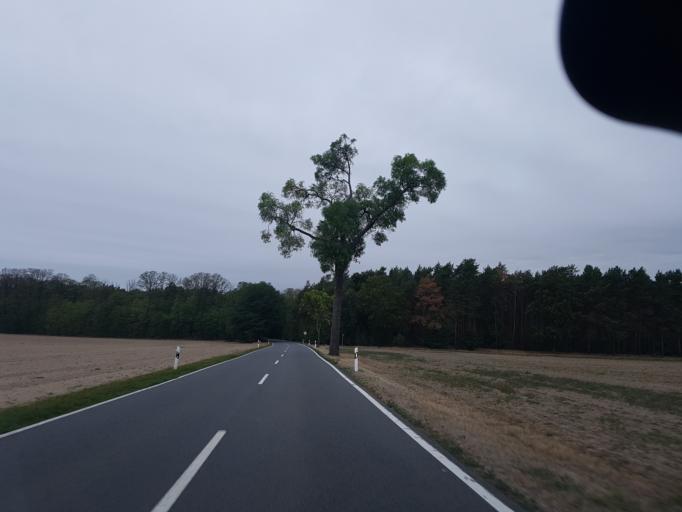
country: DE
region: Saxony-Anhalt
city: Prettin
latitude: 51.6535
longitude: 12.9618
